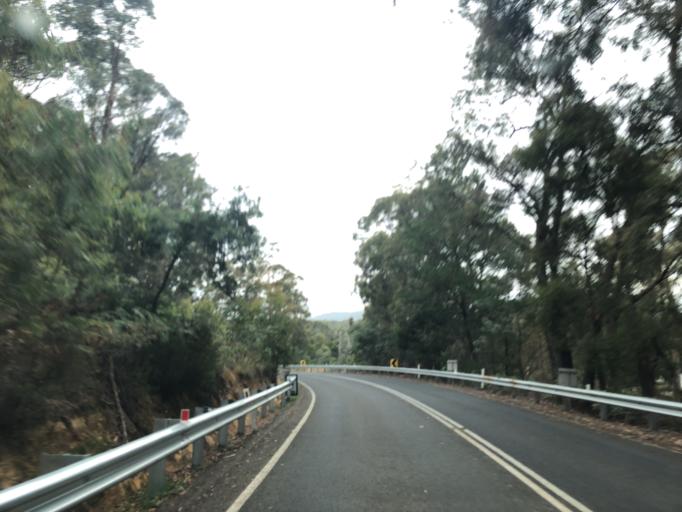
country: AU
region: Victoria
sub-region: Hume
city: Sunbury
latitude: -37.3738
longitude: 144.5082
